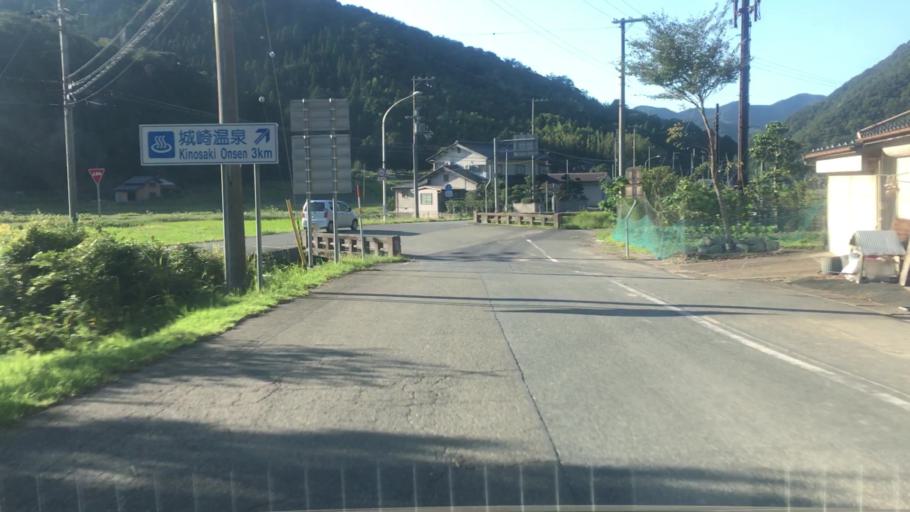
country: JP
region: Hyogo
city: Toyooka
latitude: 35.6110
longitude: 134.8293
